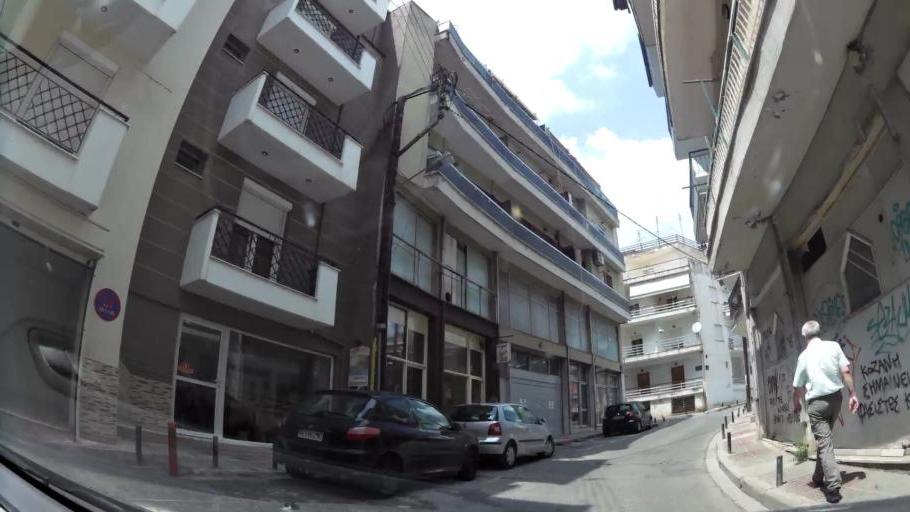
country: GR
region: West Macedonia
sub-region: Nomos Kozanis
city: Kozani
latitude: 40.3018
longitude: 21.7903
